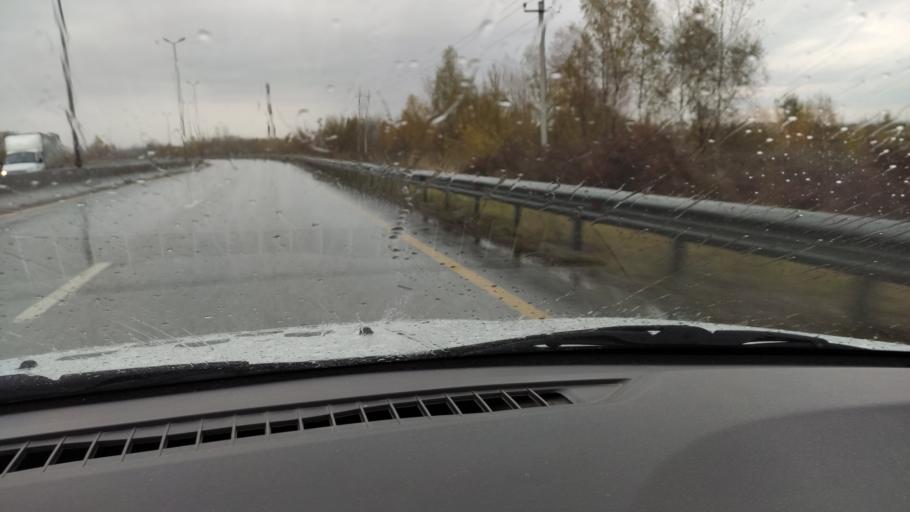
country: RU
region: Perm
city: Kondratovo
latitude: 58.0005
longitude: 56.0928
